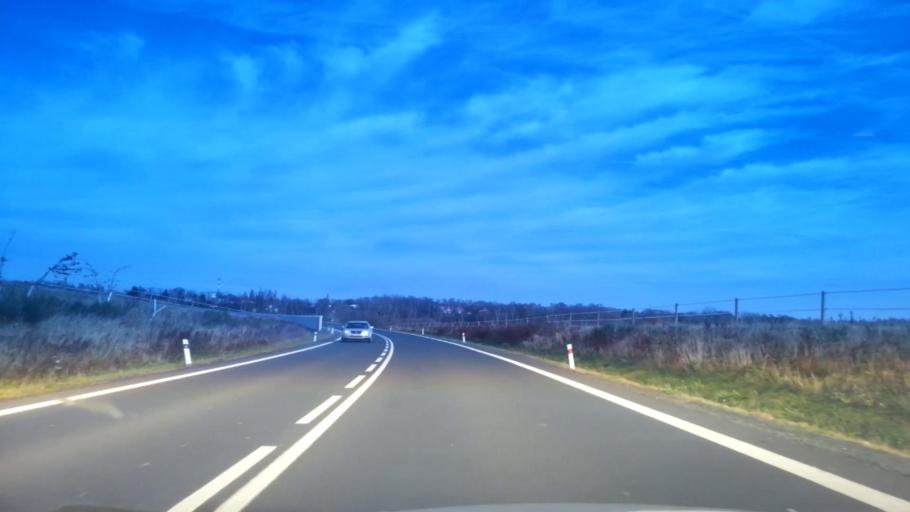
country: CZ
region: Karlovarsky
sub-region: Okres Cheb
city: Cheb
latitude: 50.0572
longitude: 12.3787
